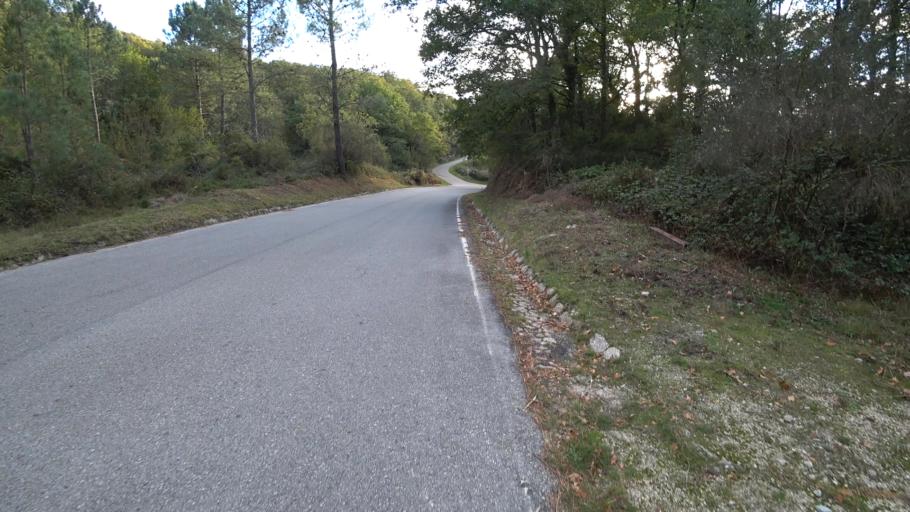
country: PT
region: Braga
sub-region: Terras de Bouro
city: Antas
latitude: 41.7645
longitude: -8.1984
